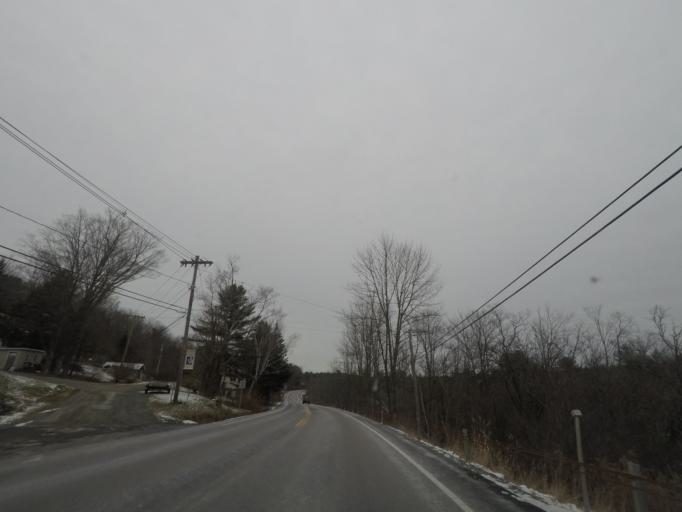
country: US
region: New York
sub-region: Rensselaer County
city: Poestenkill
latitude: 42.7697
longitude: -73.4452
